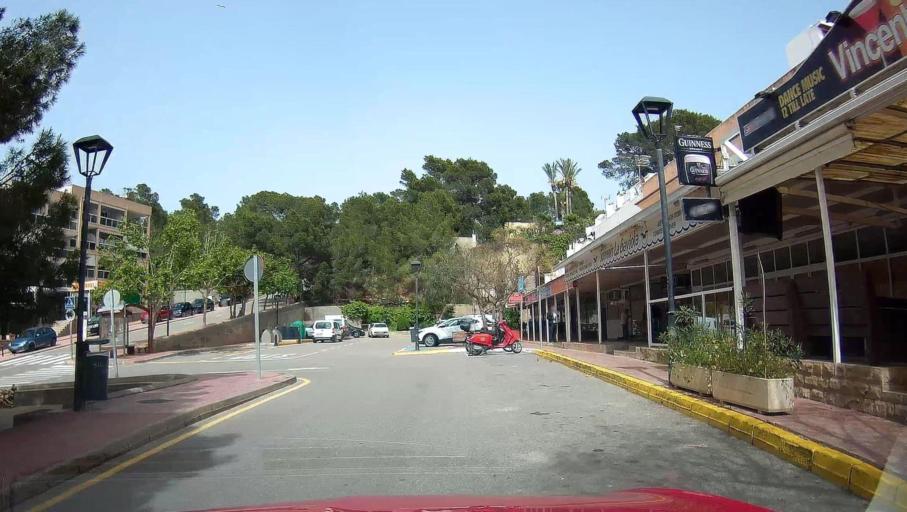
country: ES
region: Balearic Islands
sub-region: Illes Balears
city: Sant Joan de Labritja
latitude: 39.1105
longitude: 1.5183
